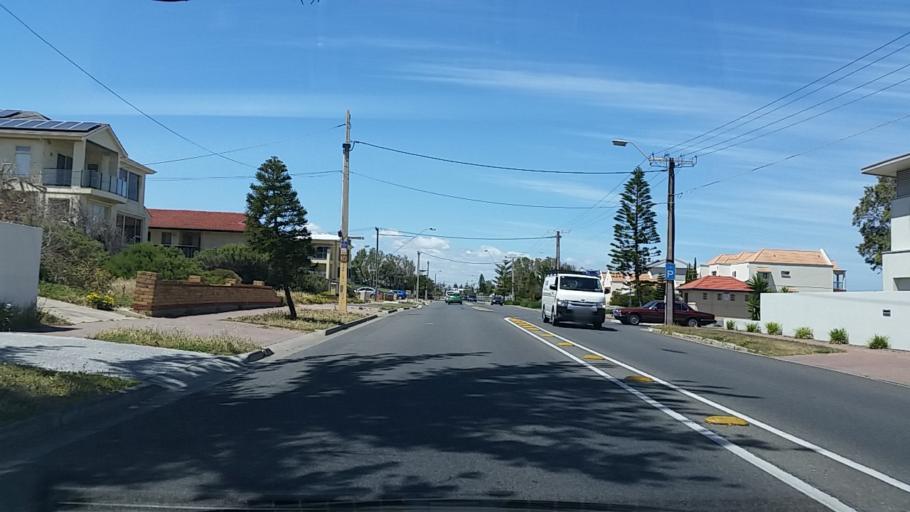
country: AU
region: South Australia
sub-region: Charles Sturt
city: Henley Beach
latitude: -34.9334
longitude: 138.4986
